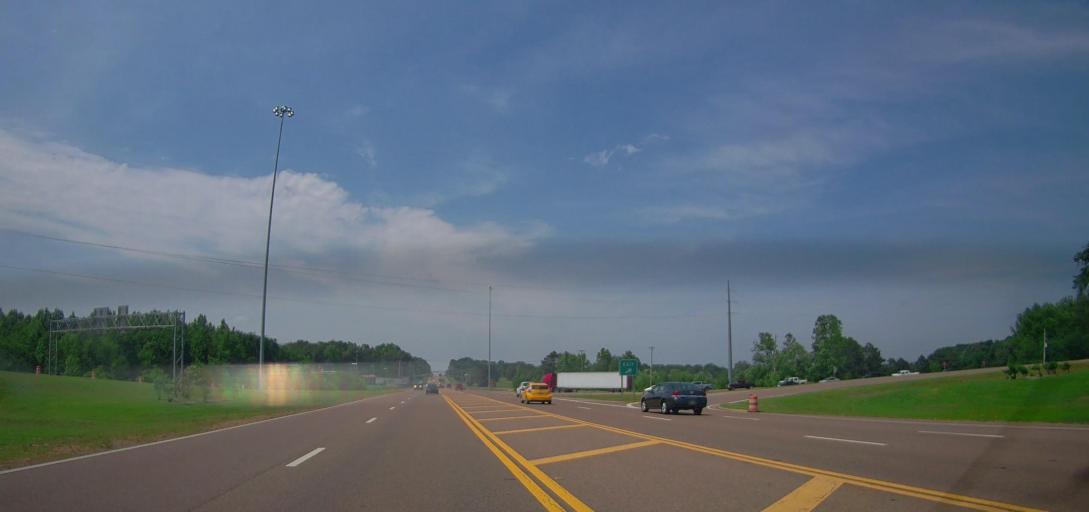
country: US
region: Mississippi
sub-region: De Soto County
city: Olive Branch
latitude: 34.9694
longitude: -89.8305
